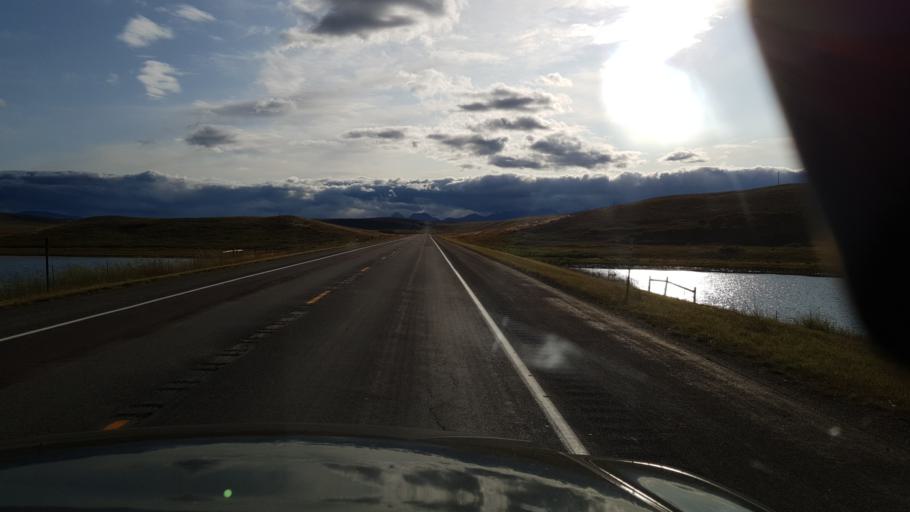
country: US
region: Montana
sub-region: Glacier County
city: South Browning
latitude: 48.5352
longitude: -113.0454
